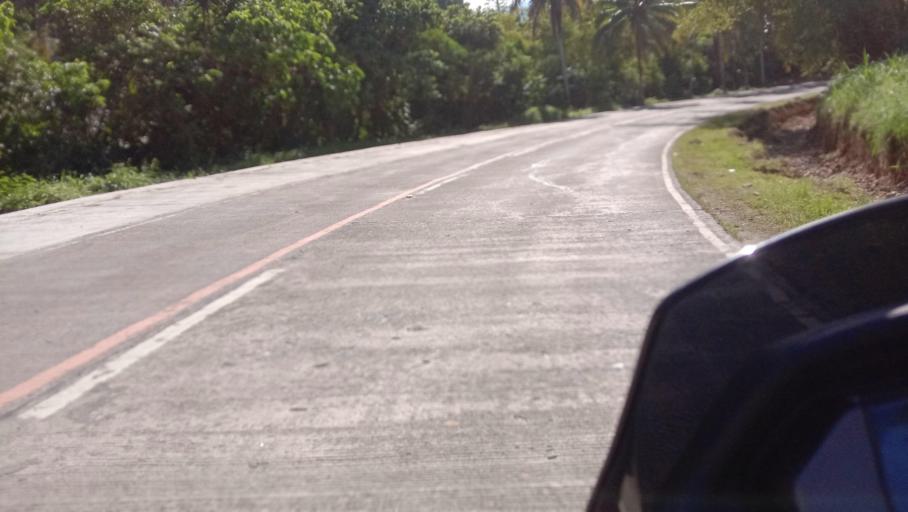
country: PH
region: Caraga
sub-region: Province of Surigao del Sur
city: Barobo
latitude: 8.5372
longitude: 126.1003
